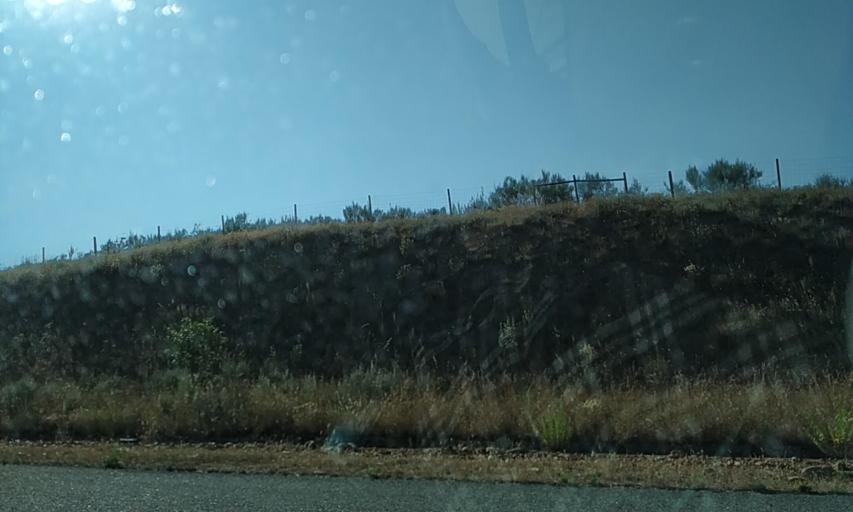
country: PT
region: Braganca
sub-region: Mirandela
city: Mirandela
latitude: 41.4784
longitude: -7.2195
